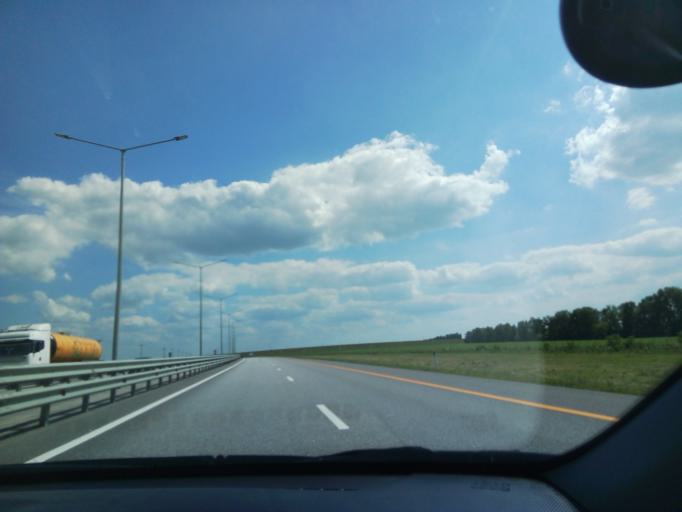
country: RU
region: Voronezj
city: Podkletnoye
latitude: 51.5130
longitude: 39.5125
